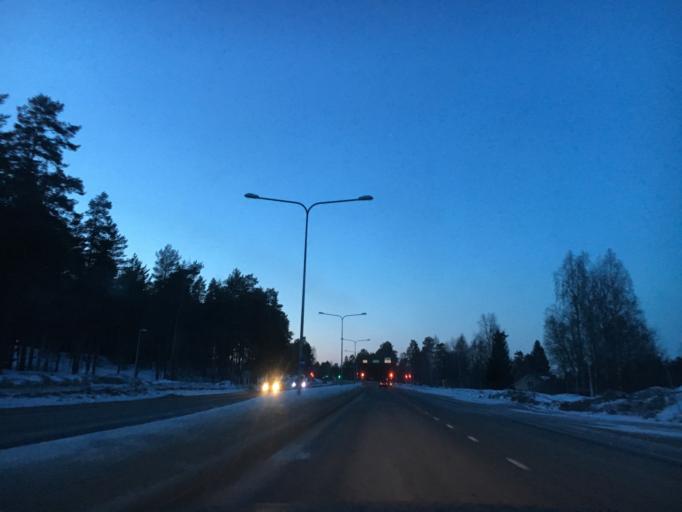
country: FI
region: Kainuu
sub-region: Kajaani
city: Kajaani
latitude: 64.2109
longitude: 27.7319
